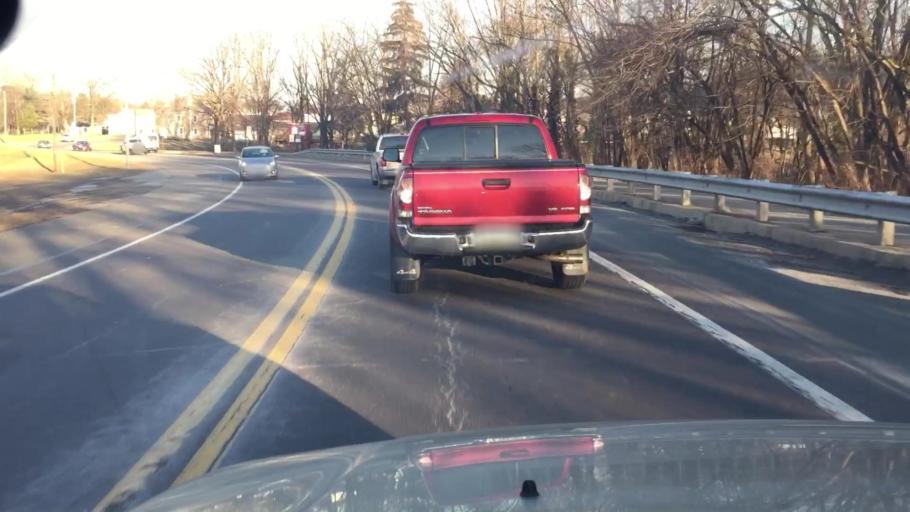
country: US
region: Pennsylvania
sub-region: Columbia County
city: Berwick
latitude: 41.0510
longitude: -76.2285
